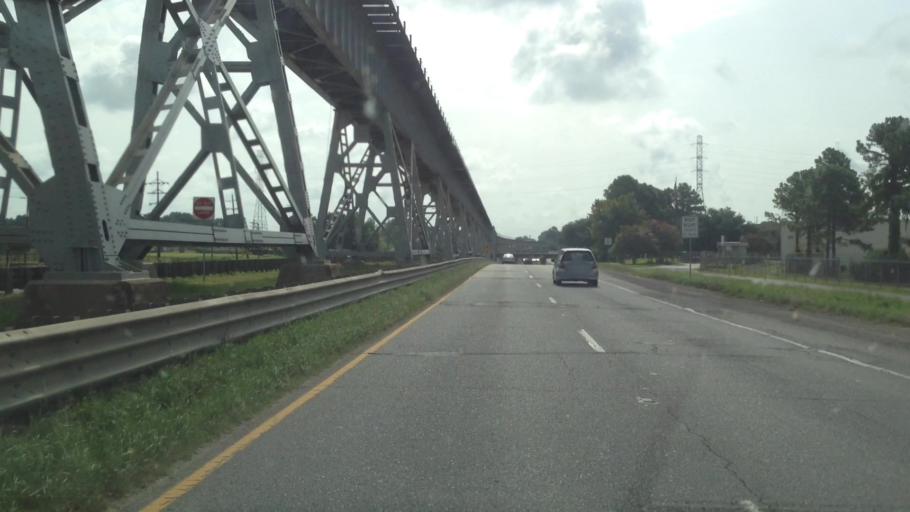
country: US
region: Louisiana
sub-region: West Baton Rouge Parish
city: Port Allen
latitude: 30.5074
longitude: -91.1875
